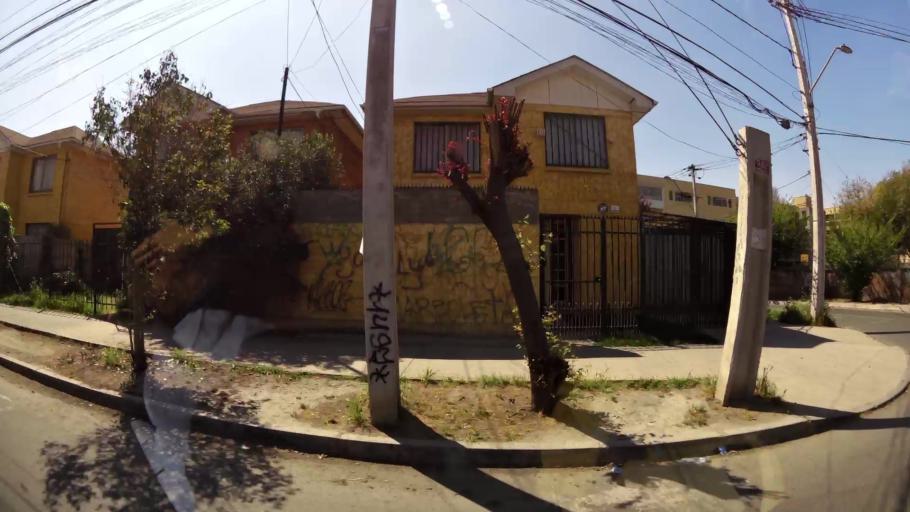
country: CL
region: Santiago Metropolitan
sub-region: Provincia de Santiago
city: Lo Prado
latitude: -33.3583
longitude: -70.7222
